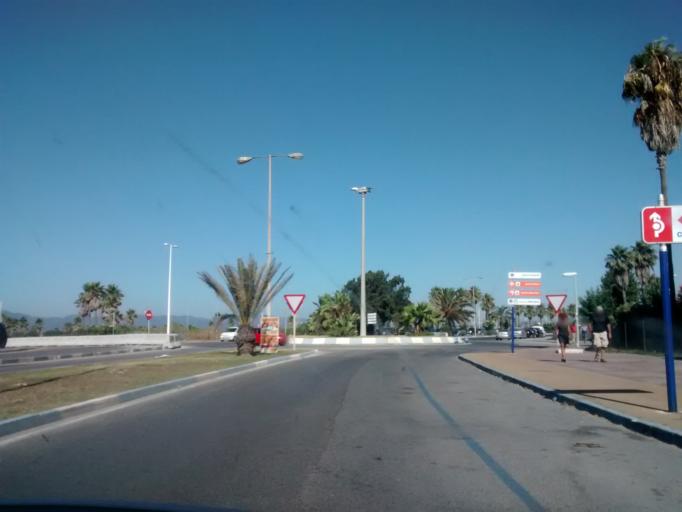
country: GI
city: Gibraltar
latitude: 36.1562
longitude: -5.3510
